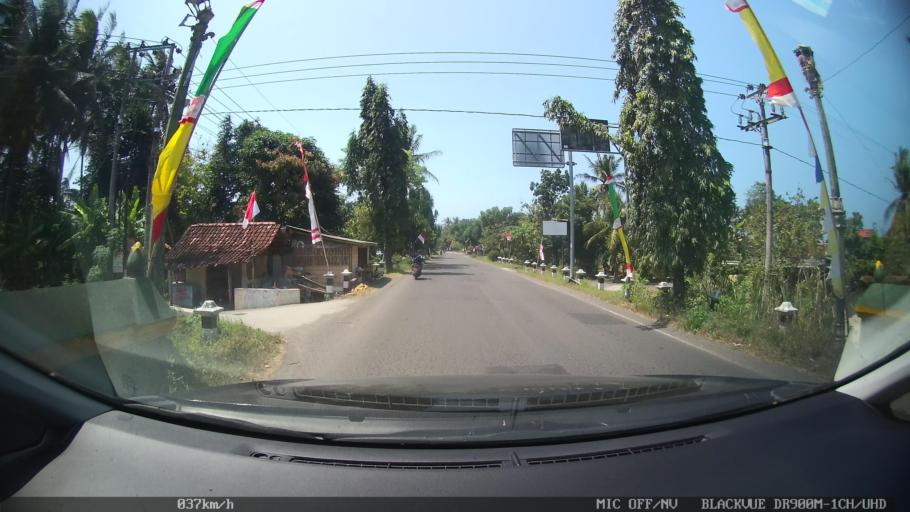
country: ID
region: Daerah Istimewa Yogyakarta
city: Srandakan
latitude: -7.9085
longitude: 110.0839
